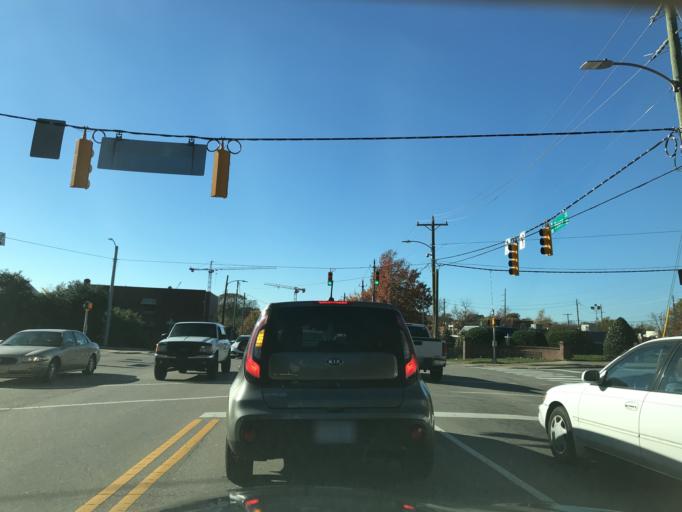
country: US
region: North Carolina
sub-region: Wake County
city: Raleigh
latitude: 35.7880
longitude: -78.6383
